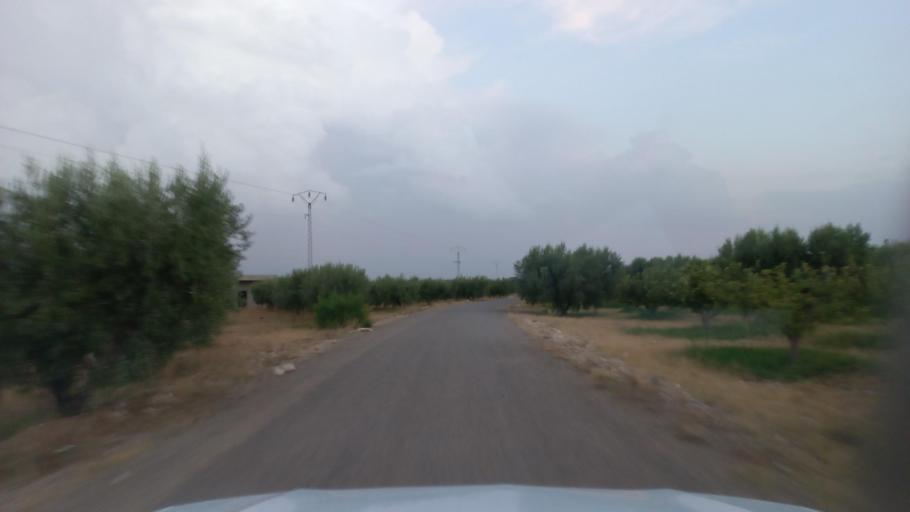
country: TN
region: Al Qasrayn
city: Kasserine
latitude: 35.2725
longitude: 9.0369
